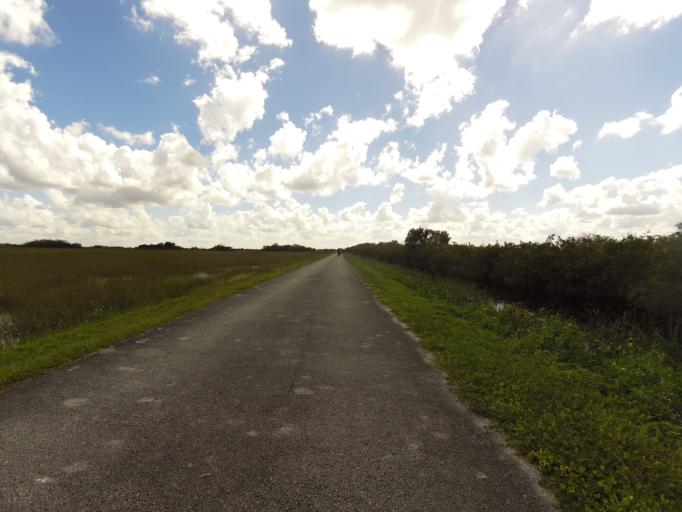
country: US
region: Florida
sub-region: Miami-Dade County
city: The Hammocks
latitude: 25.7204
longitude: -80.7667
